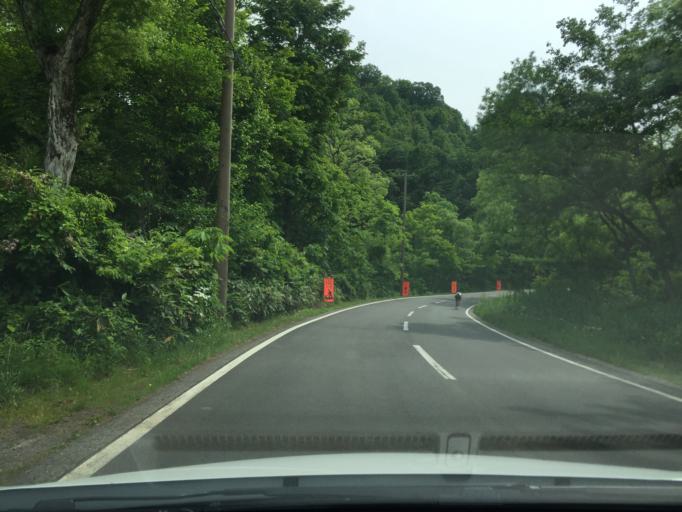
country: JP
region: Fukushima
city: Inawashiro
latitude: 37.6424
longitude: 140.0485
